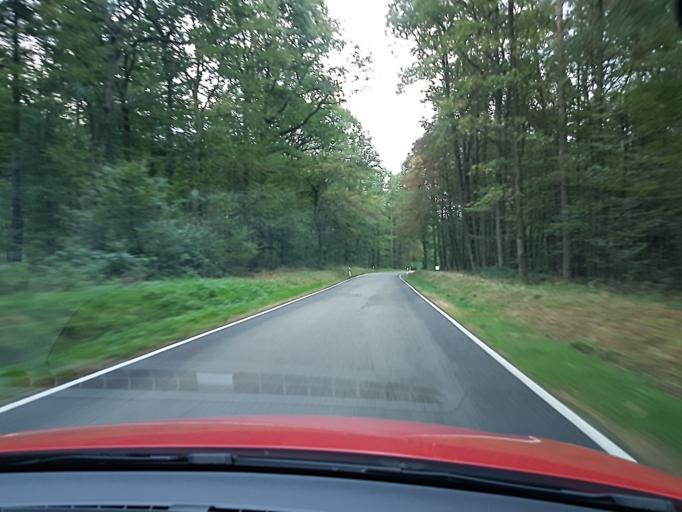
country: DE
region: Baden-Wuerttemberg
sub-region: Karlsruhe Region
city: Sternenfels
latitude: 49.0431
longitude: 8.8687
